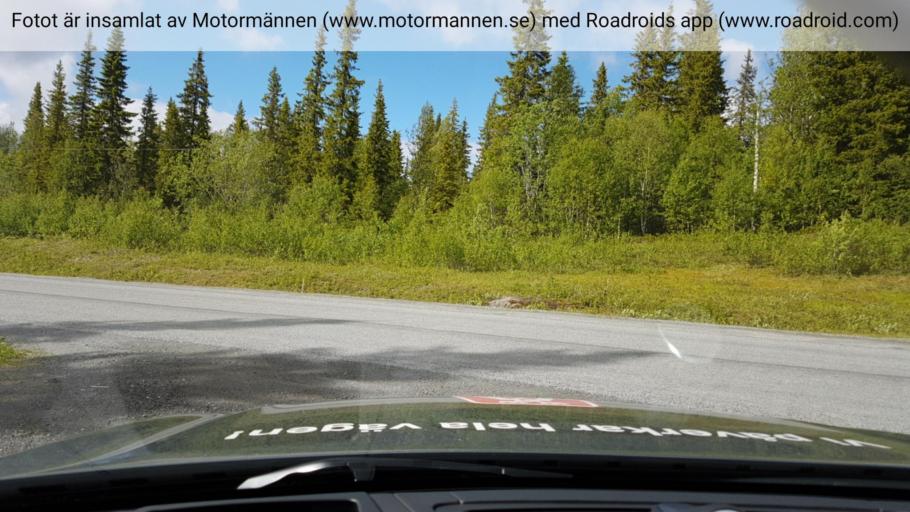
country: SE
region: Jaemtland
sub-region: Are Kommun
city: Are
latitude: 63.7038
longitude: 12.7615
